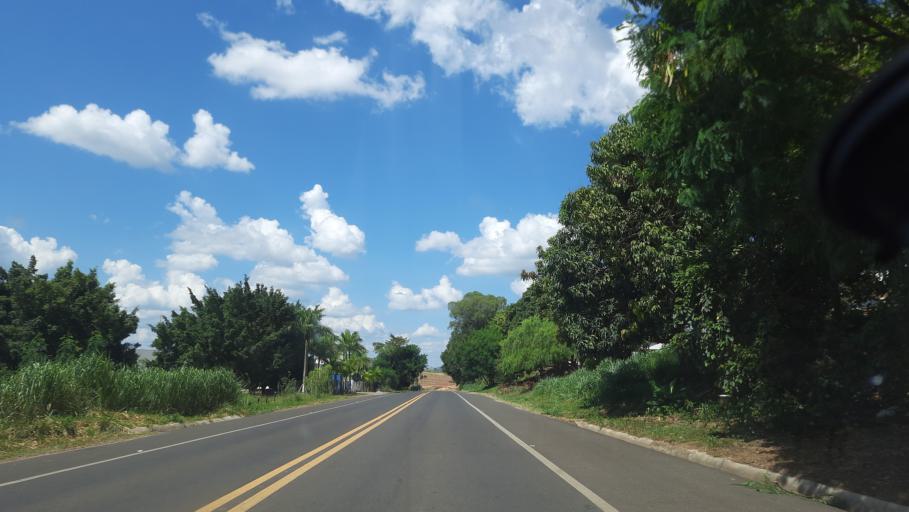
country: BR
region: Sao Paulo
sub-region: Sao Jose Do Rio Pardo
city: Sao Jose do Rio Pardo
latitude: -21.6055
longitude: -46.9301
